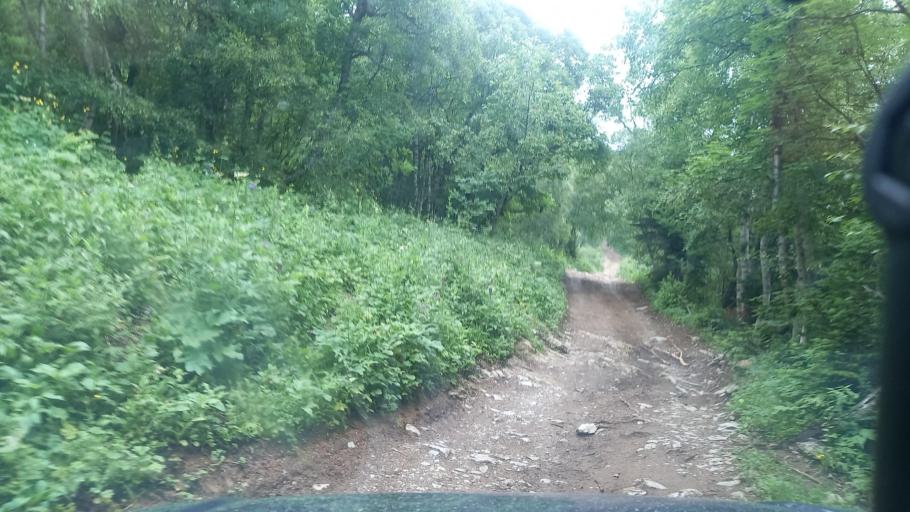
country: RU
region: Karachayevo-Cherkesiya
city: Kurdzhinovo
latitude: 43.7990
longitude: 40.8435
